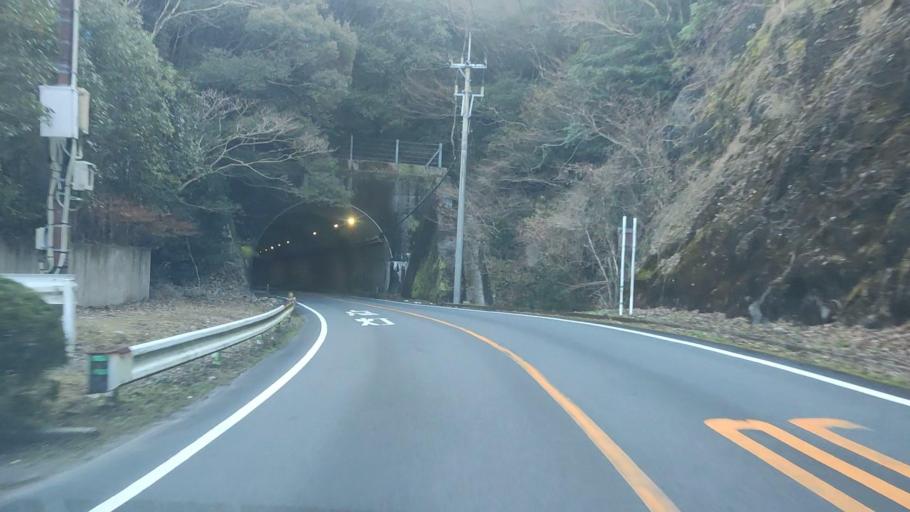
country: JP
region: Miyazaki
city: Nobeoka
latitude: 32.6319
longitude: 131.7284
